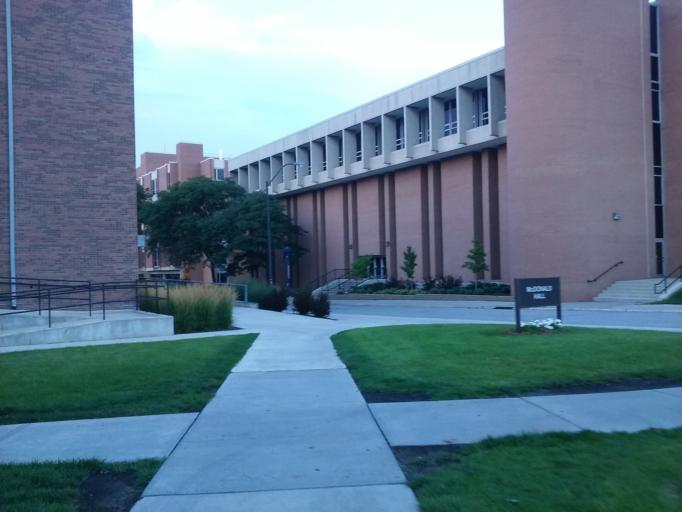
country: US
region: Ohio
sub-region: Wood County
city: Bowling Green
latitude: 41.3787
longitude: -83.6413
